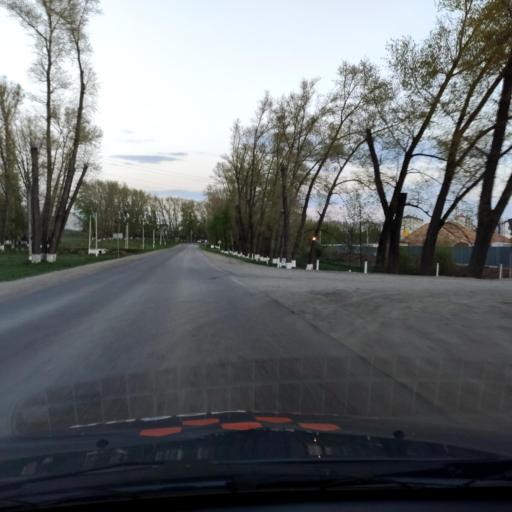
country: RU
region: Voronezj
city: Novaya Usman'
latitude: 51.6771
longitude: 39.4051
